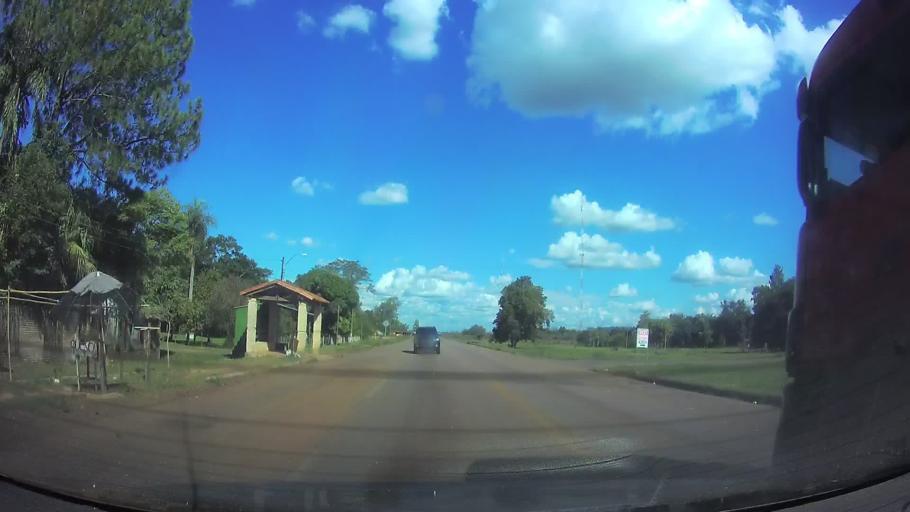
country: PY
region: Paraguari
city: Sapucai
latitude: -25.6930
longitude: -56.8605
